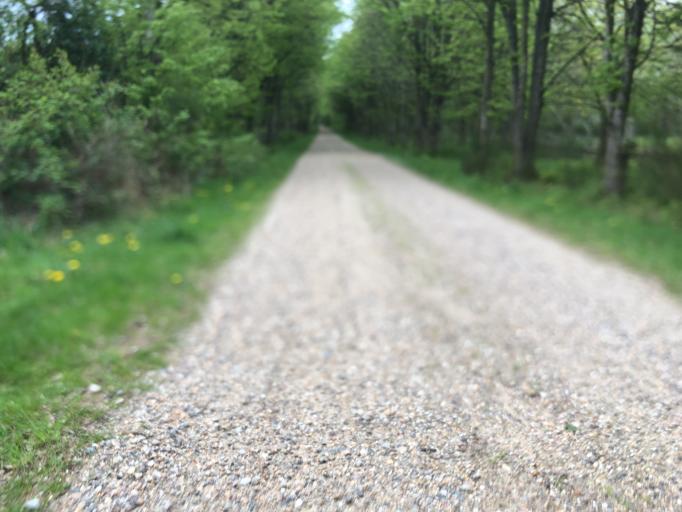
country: DK
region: Central Jutland
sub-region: Holstebro Kommune
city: Ulfborg
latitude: 56.2709
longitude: 8.4296
